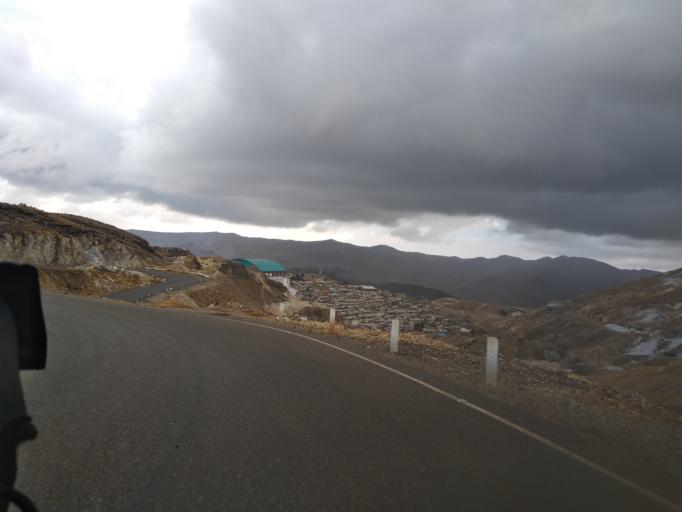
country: PE
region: La Libertad
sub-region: Provincia de Santiago de Chuco
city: Quiruvilca
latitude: -7.9972
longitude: -78.3072
